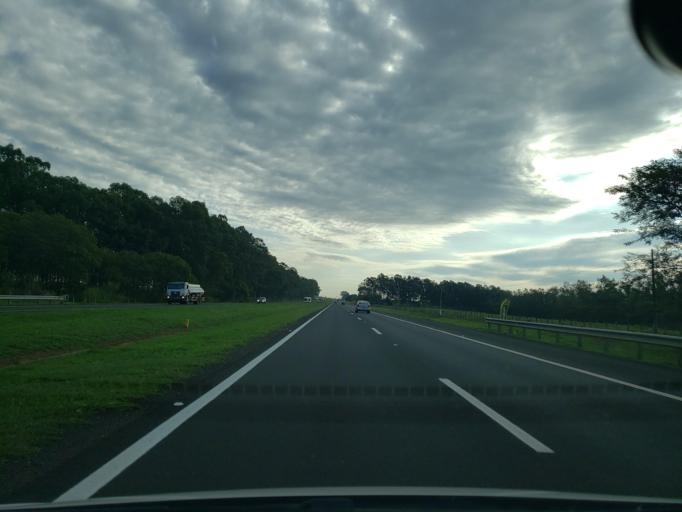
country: BR
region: Sao Paulo
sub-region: Guararapes
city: Guararapes
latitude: -21.2145
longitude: -50.6959
